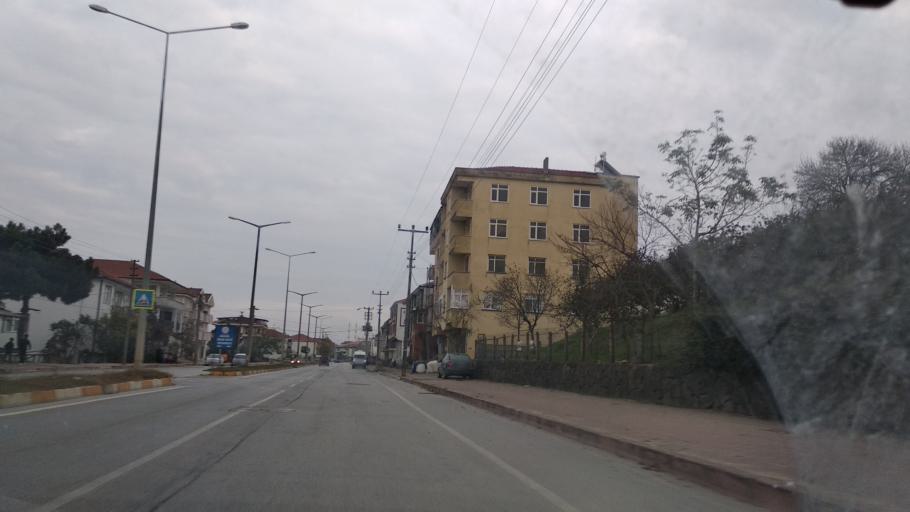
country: TR
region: Sakarya
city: Karasu
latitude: 41.0966
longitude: 30.6801
